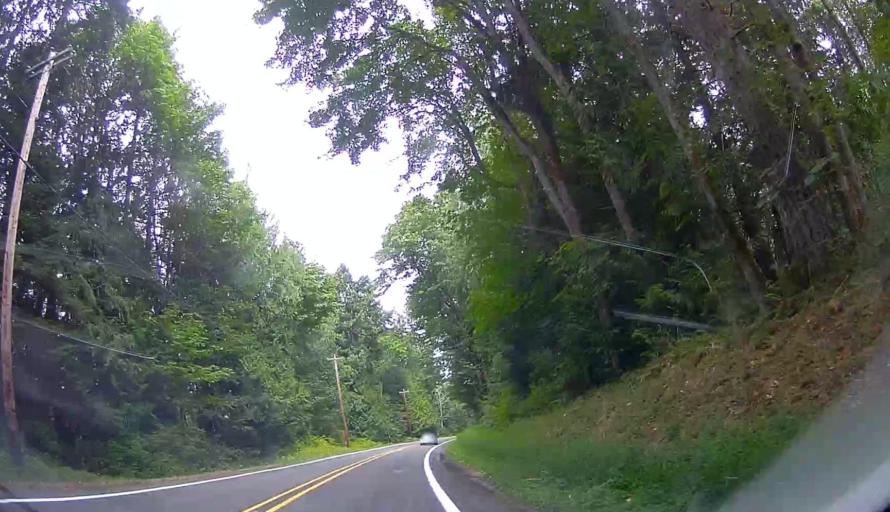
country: US
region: Washington
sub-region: Snohomish County
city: Warm Beach
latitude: 48.1351
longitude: -122.3609
